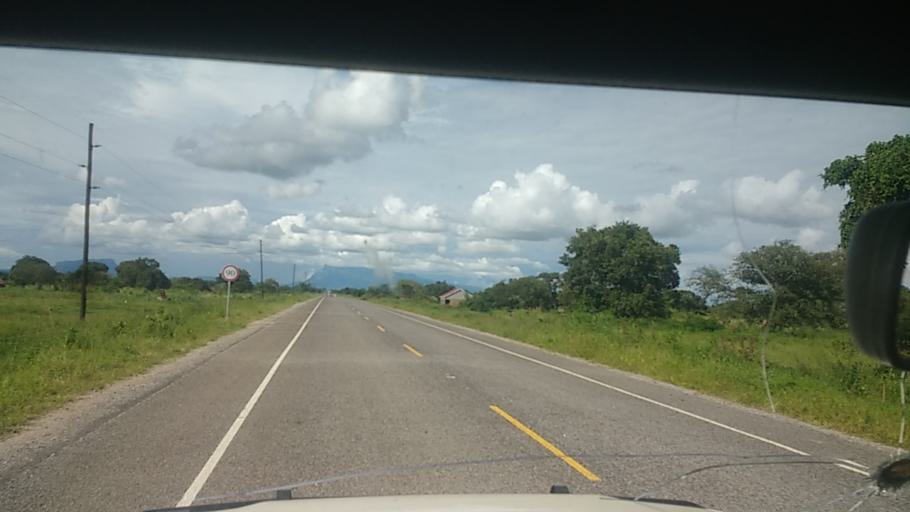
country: UG
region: Eastern Region
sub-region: Katakwi District
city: Katakwi
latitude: 1.9153
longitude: 34.0418
